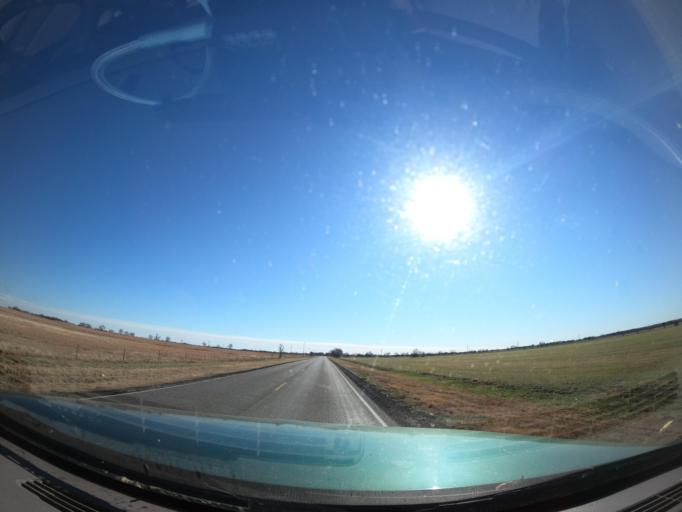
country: US
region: Oklahoma
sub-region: McIntosh County
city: Checotah
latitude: 35.5853
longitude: -95.6599
